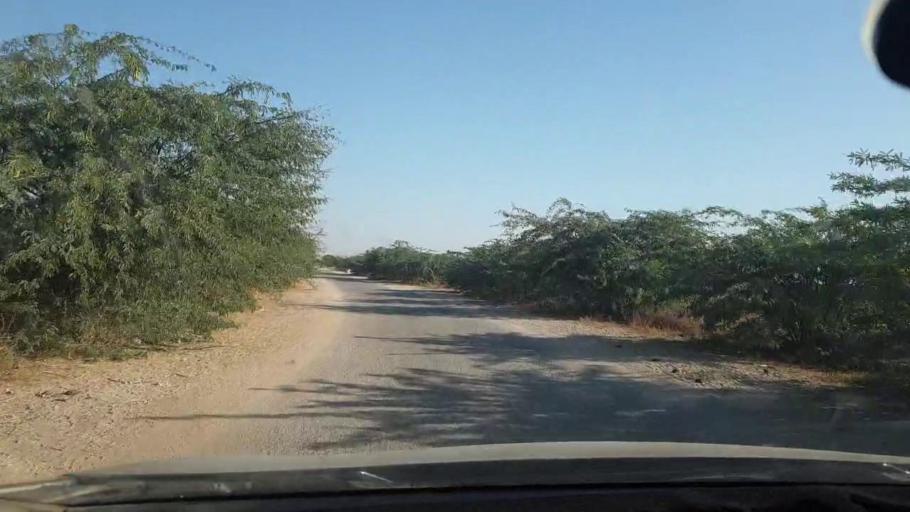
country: PK
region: Sindh
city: Malir Cantonment
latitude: 25.1700
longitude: 67.2005
